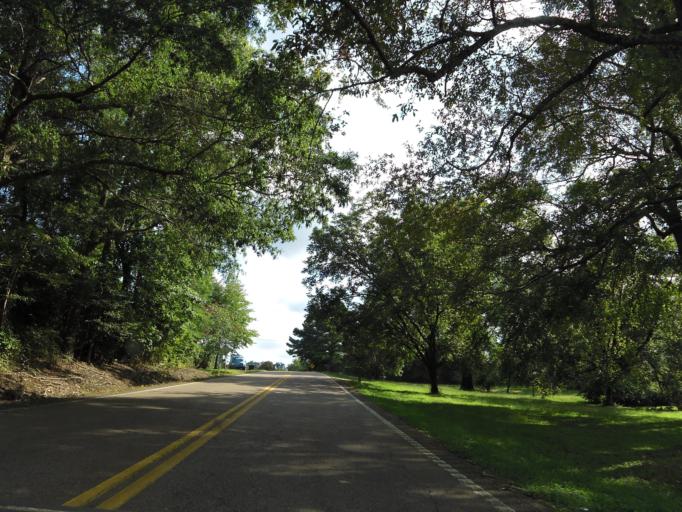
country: US
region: Mississippi
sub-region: Alcorn County
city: Farmington
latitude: 35.0664
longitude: -88.3943
